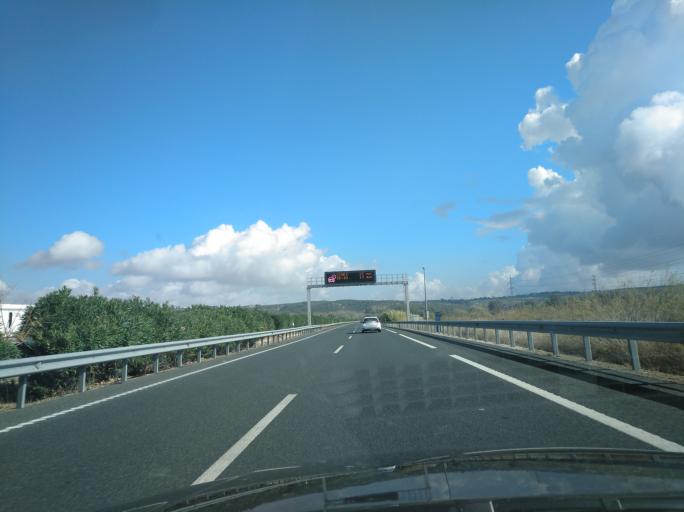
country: ES
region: Andalusia
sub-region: Provincia de Sevilla
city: Sanlucar la Mayor
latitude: 37.3698
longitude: -6.2373
